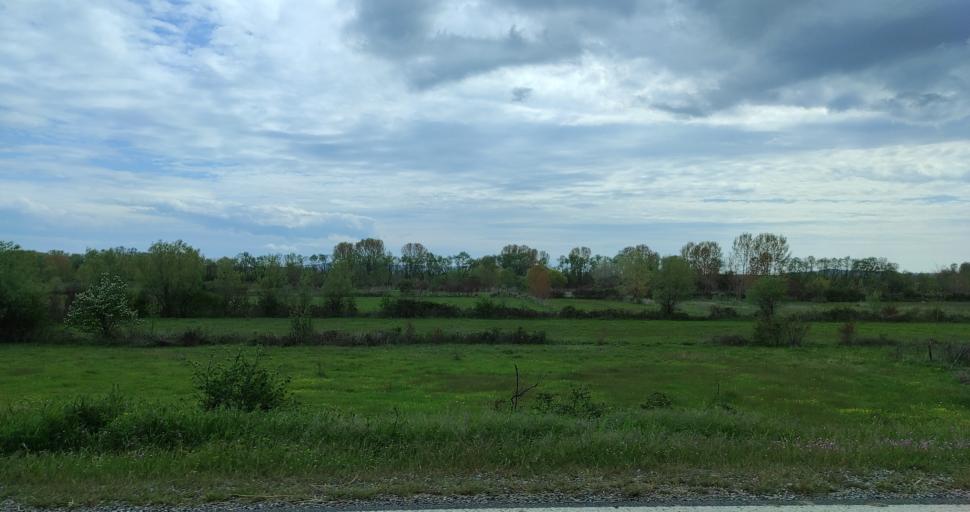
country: AL
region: Shkoder
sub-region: Rrethi i Shkodres
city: Dajc
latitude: 42.0111
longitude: 19.4139
